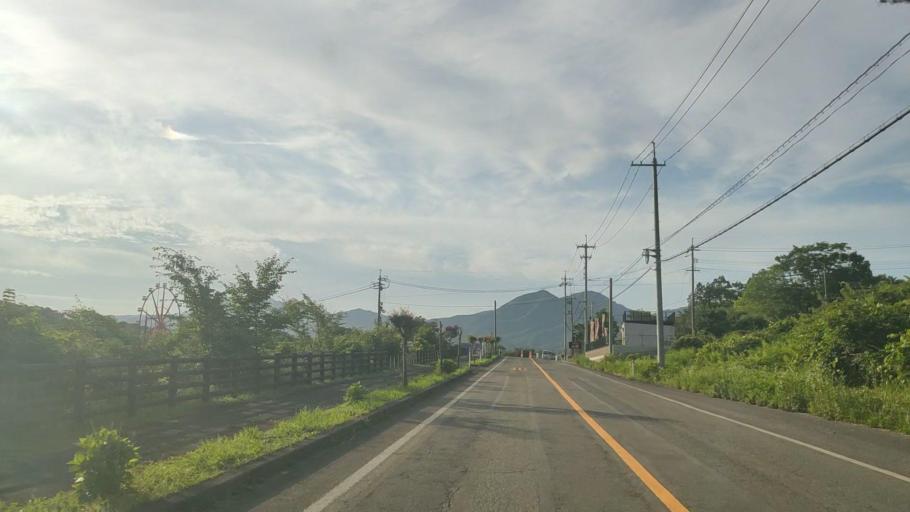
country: JP
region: Tottori
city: Kurayoshi
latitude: 35.2883
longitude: 133.6371
